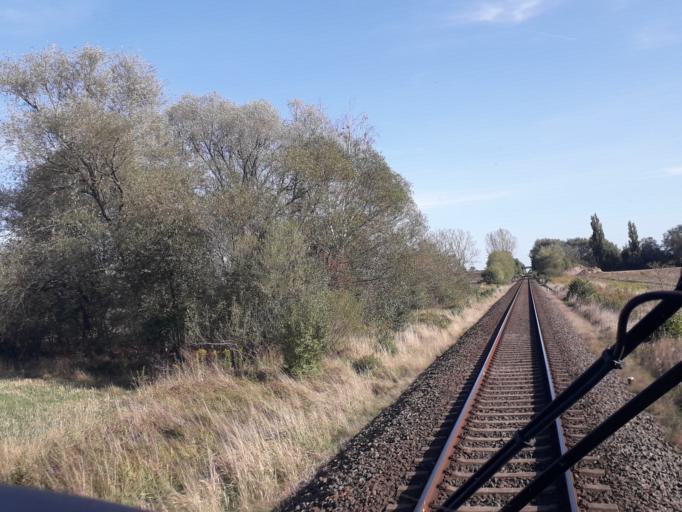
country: DE
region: Brandenburg
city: Velten
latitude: 52.7123
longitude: 13.1311
